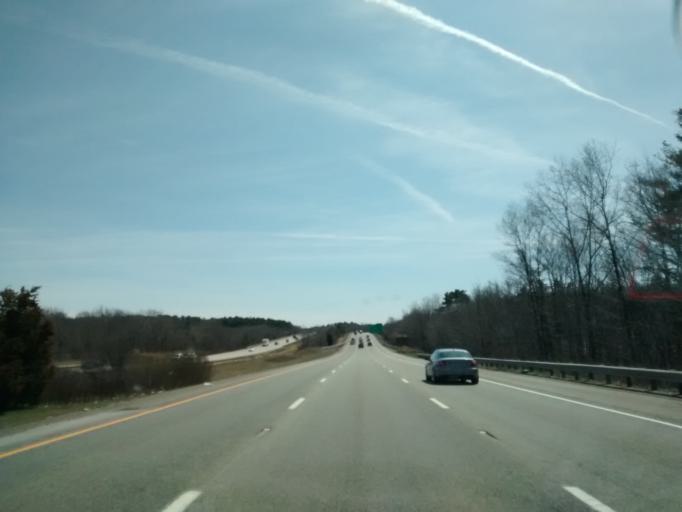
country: US
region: Massachusetts
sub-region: Worcester County
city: Cordaville
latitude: 42.2736
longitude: -71.5658
